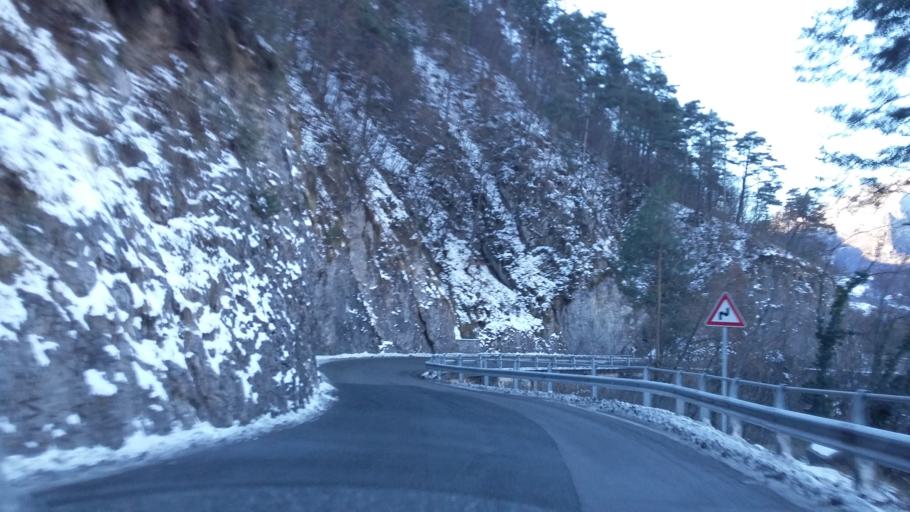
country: IT
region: Lombardy
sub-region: Provincia di Brescia
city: Ponte Caffaro
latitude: 45.8224
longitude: 10.5081
